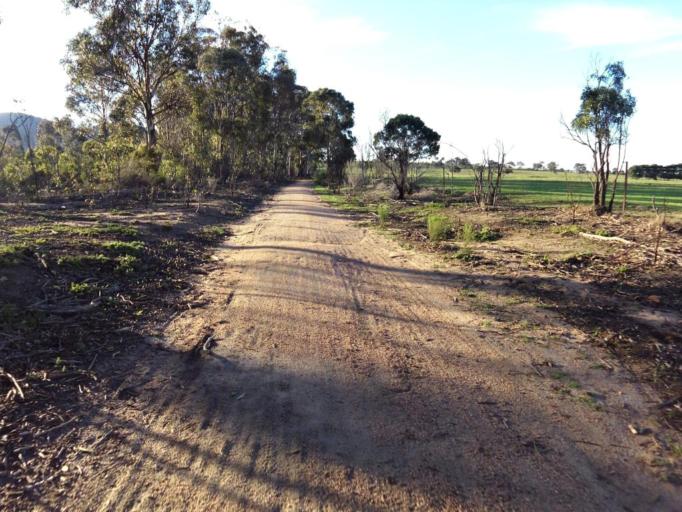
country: AU
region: Victoria
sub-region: Wyndham
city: Little River
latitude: -37.9608
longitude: 144.4446
